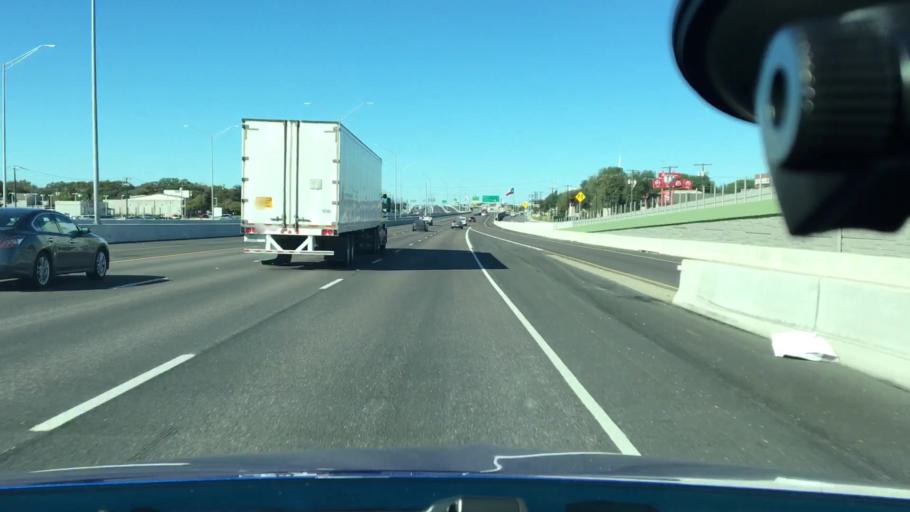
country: US
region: Texas
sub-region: Dallas County
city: Irving
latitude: 32.8371
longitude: -96.9634
